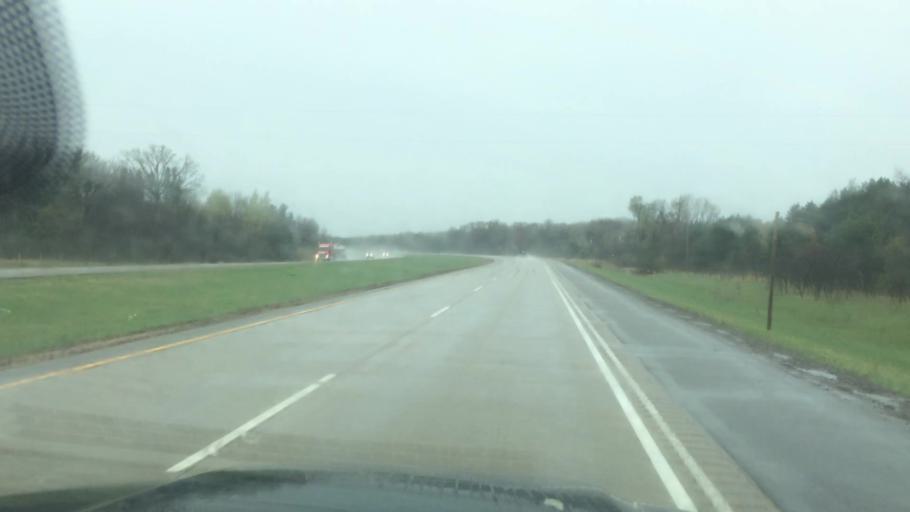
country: US
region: Wisconsin
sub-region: Marathon County
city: Mosinee
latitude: 44.6641
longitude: -89.6431
